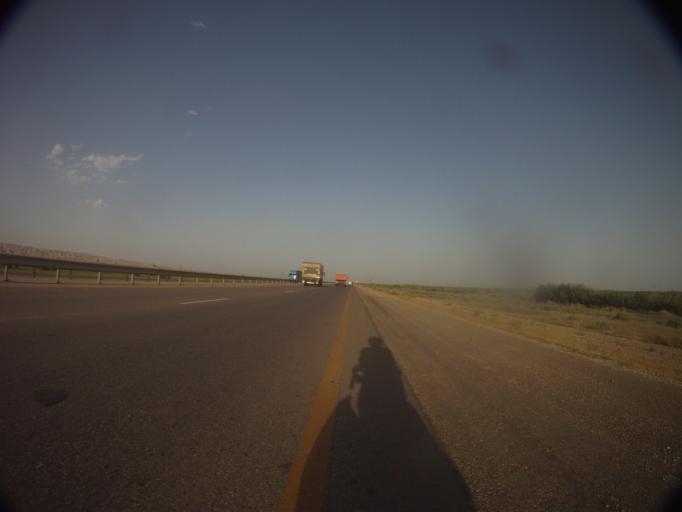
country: AZ
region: Goranboy
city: Qizilhacili
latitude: 40.6427
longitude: 46.8855
